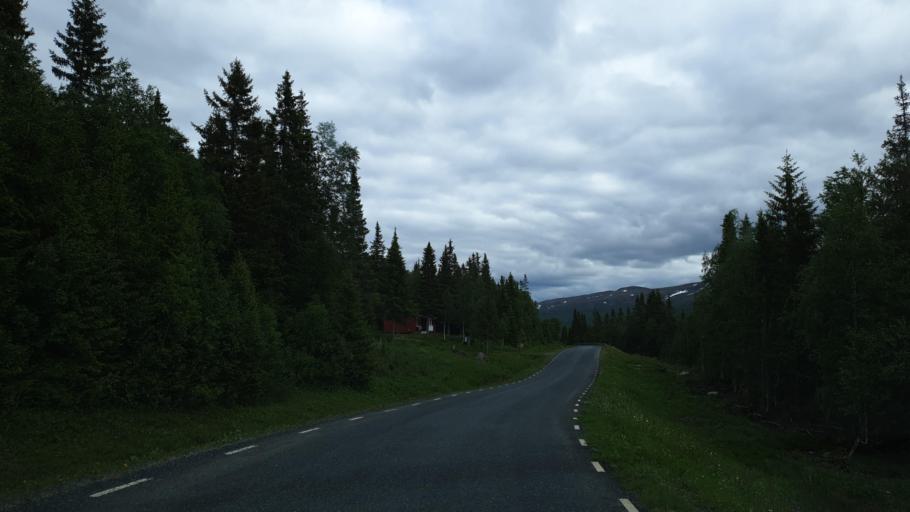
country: NO
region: Nordland
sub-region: Hattfjelldal
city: Hattfjelldal
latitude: 65.4430
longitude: 14.5449
